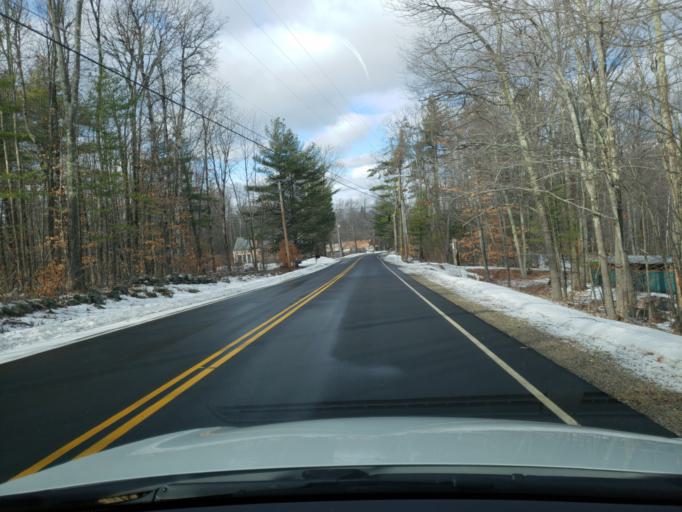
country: US
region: New Hampshire
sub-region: Hillsborough County
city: Greenfield
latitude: 43.0091
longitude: -71.8497
